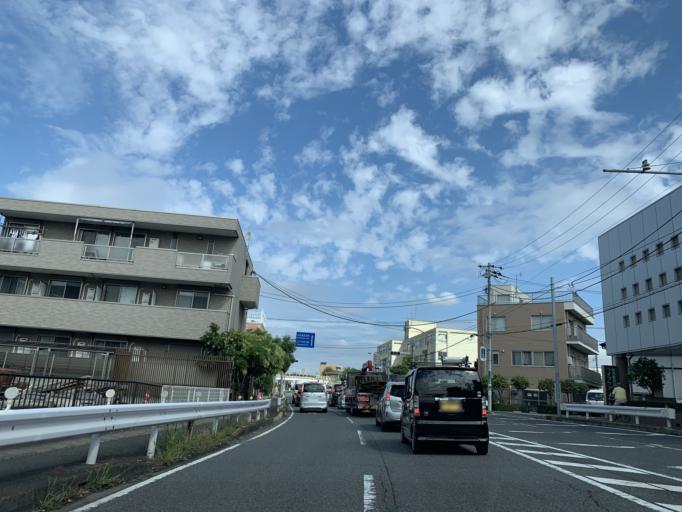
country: JP
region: Tokyo
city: Urayasu
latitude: 35.6913
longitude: 139.9228
